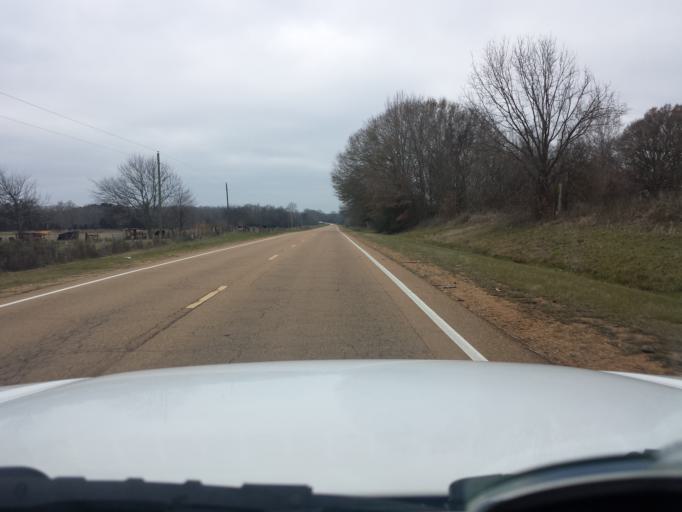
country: US
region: Mississippi
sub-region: Madison County
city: Canton
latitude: 32.7609
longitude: -90.1612
